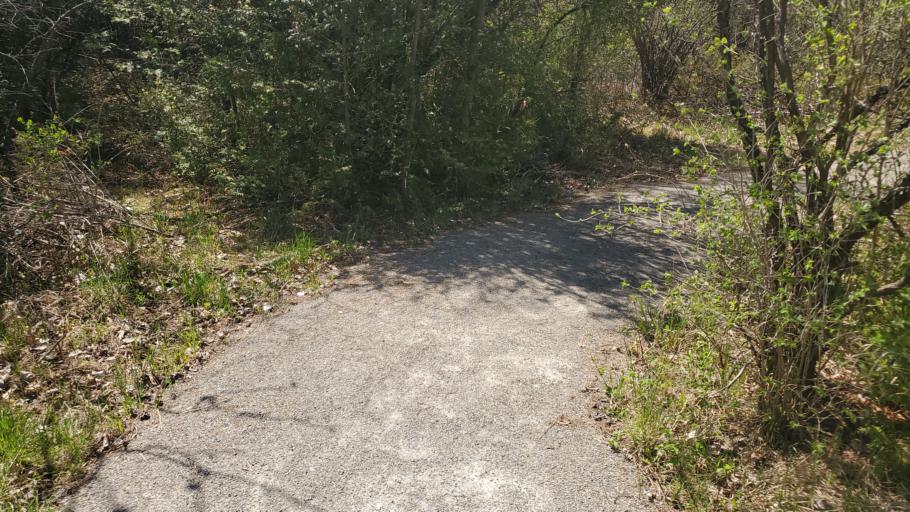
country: CA
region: Ontario
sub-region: Lanark County
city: Smiths Falls
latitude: 44.9133
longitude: -75.8299
